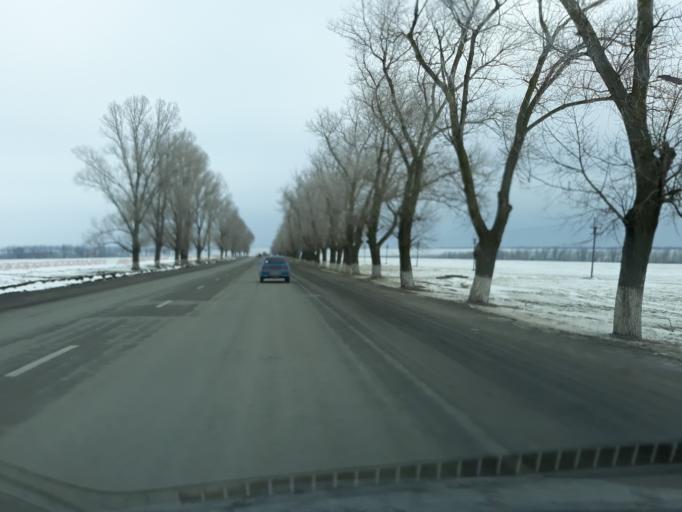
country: RU
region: Rostov
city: Primorka
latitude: 47.3171
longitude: 39.0969
